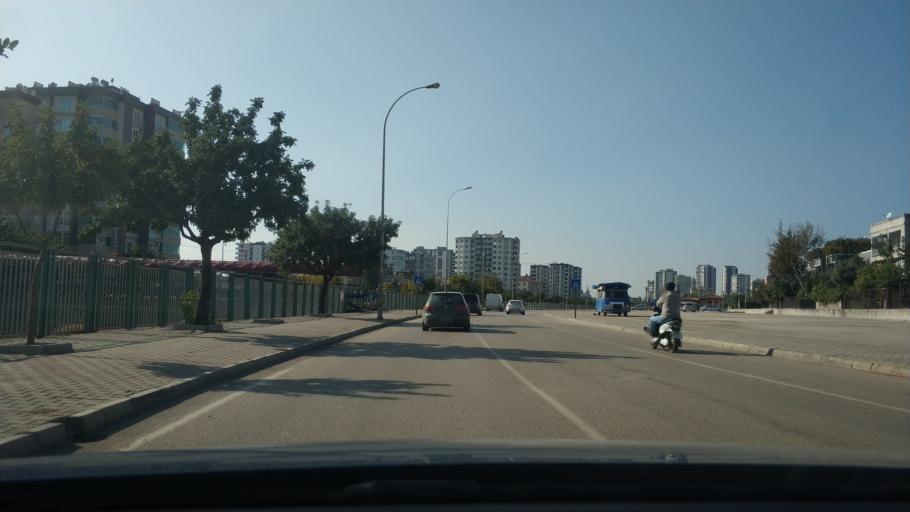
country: TR
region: Adana
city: Seyhan
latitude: 37.0110
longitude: 35.3016
